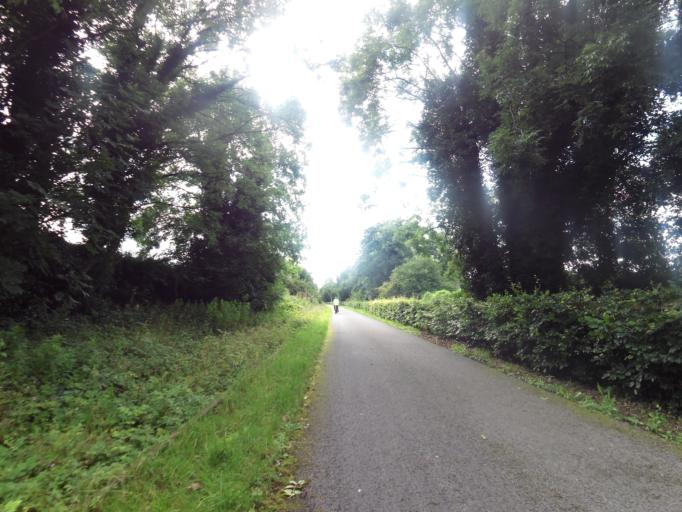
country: IE
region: Leinster
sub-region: An Iarmhi
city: An Muileann gCearr
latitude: 53.5072
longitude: -7.4169
